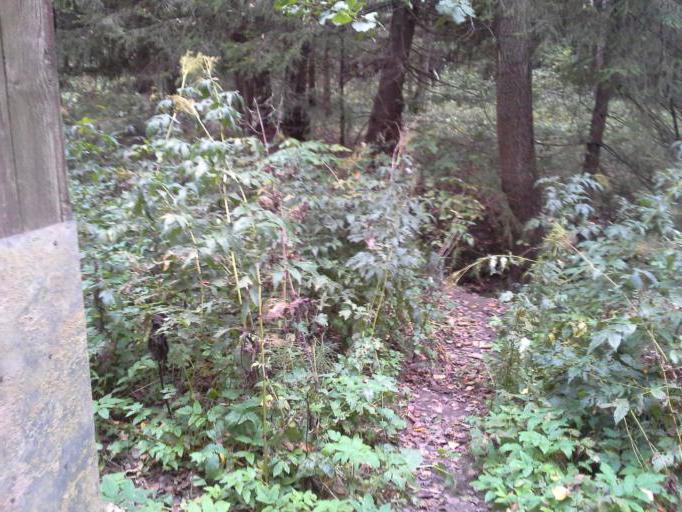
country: RU
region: Moskovskaya
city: Krasnoznamensk
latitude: 55.6249
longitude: 37.0640
